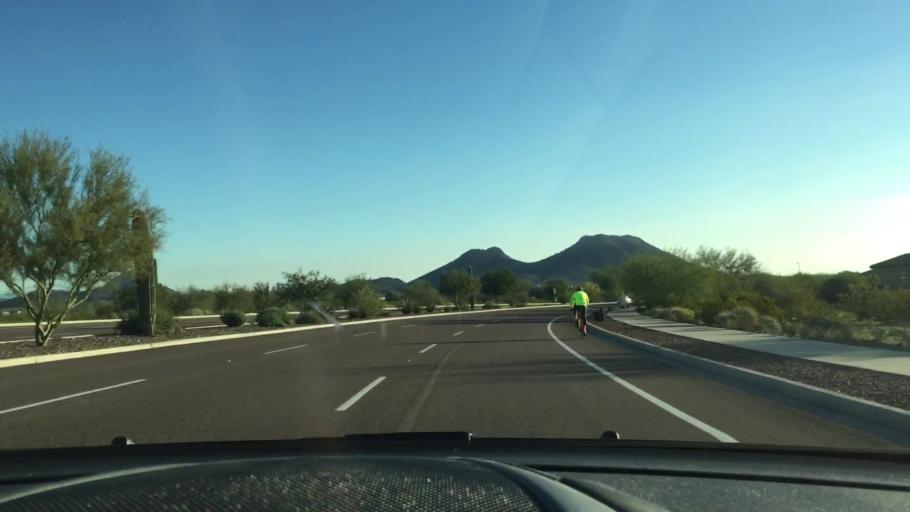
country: US
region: Arizona
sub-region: Maricopa County
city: Sun City
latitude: 33.7104
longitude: -112.2295
